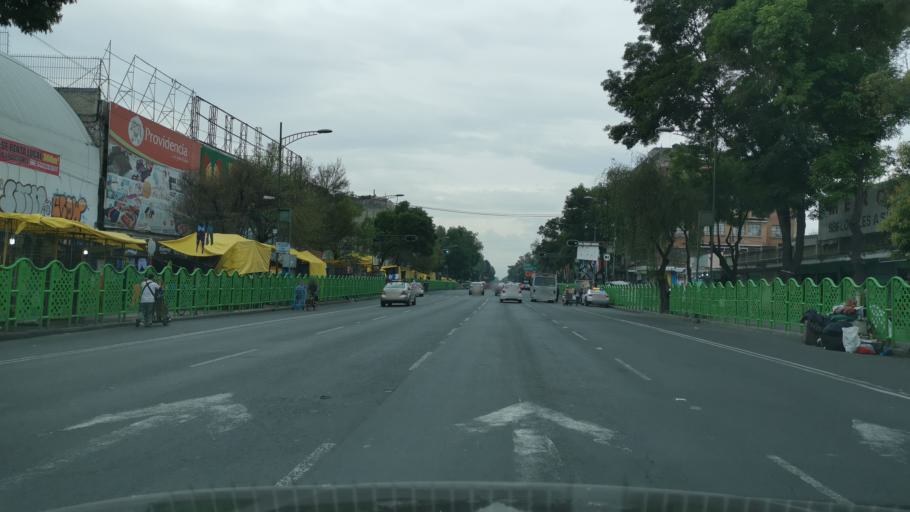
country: MX
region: Mexico City
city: Mexico City
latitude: 19.4346
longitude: -99.1242
